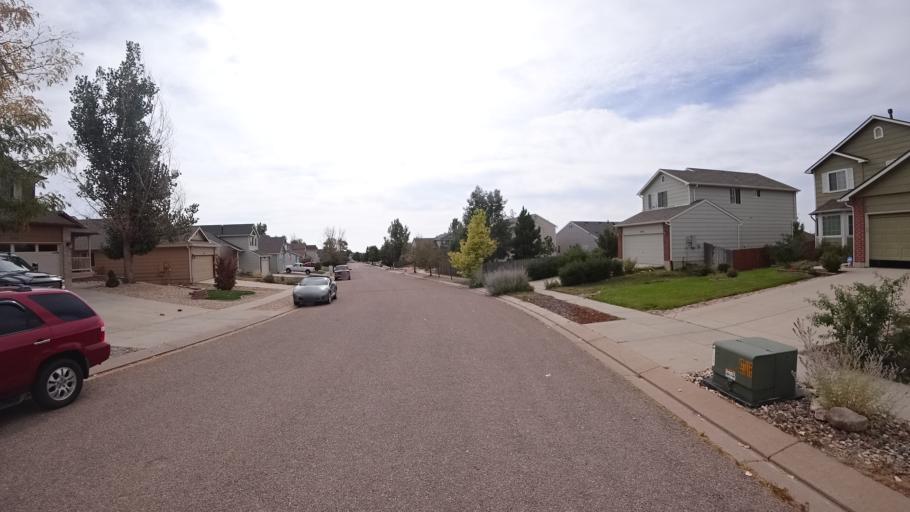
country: US
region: Colorado
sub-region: El Paso County
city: Cimarron Hills
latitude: 38.9153
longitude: -104.7150
